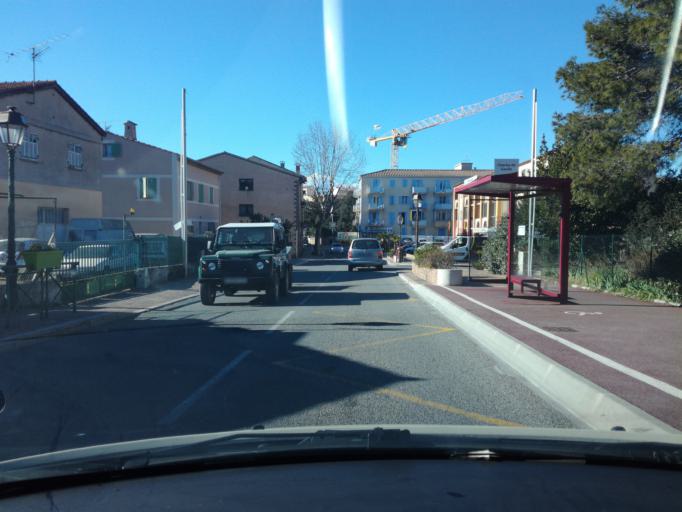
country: FR
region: Provence-Alpes-Cote d'Azur
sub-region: Departement du Var
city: Puget-sur-Argens
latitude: 43.4537
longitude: 6.6893
